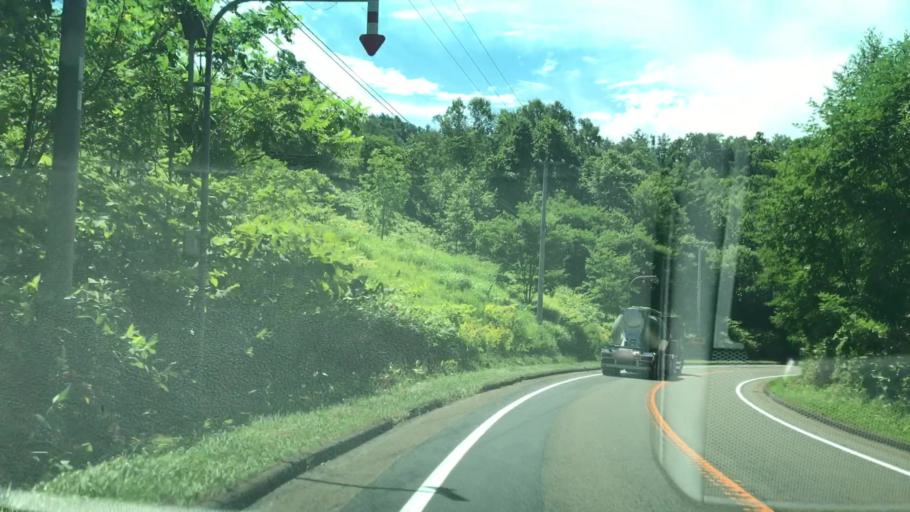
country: JP
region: Hokkaido
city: Shimo-furano
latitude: 42.9021
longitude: 142.4384
